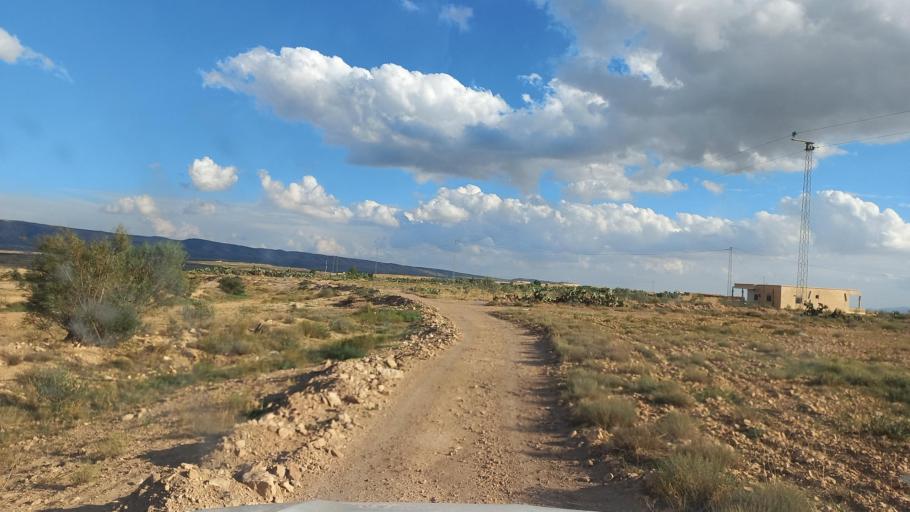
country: TN
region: Al Qasrayn
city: Sbiba
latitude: 35.3834
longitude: 9.0698
